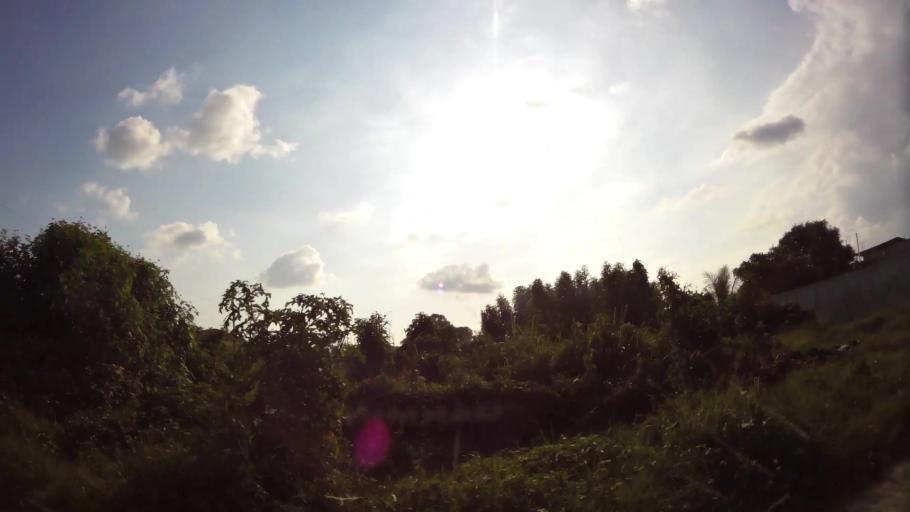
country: GT
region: Retalhuleu
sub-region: Municipio de Retalhuleu
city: Retalhuleu
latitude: 14.5309
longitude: -91.6753
